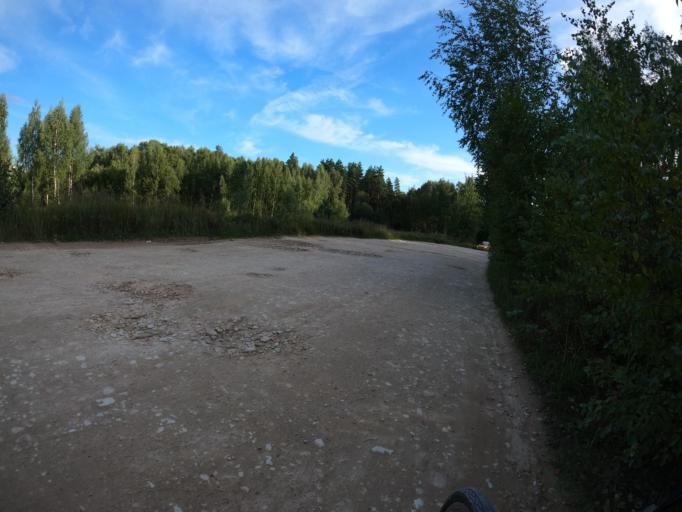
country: RU
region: Moskovskaya
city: Meshcherino
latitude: 55.1369
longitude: 38.3967
